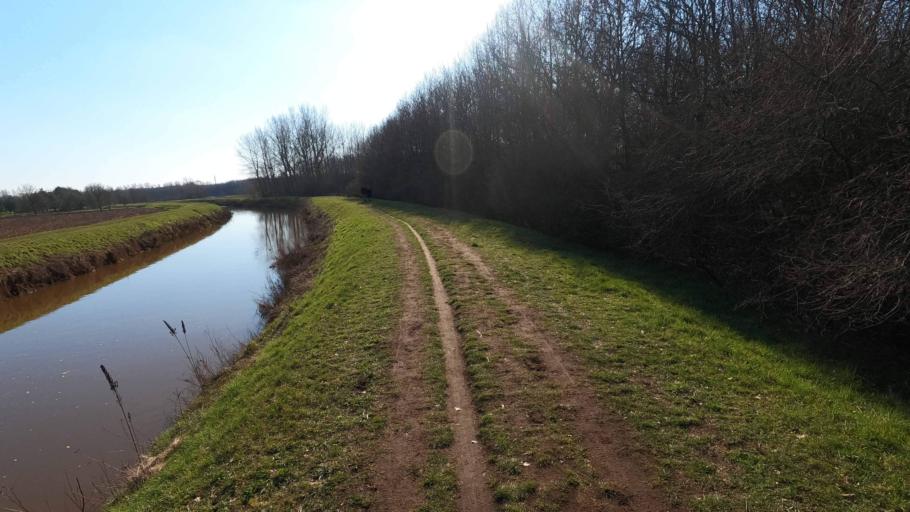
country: BE
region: Flanders
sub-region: Provincie Antwerpen
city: Herenthout
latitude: 51.1161
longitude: 4.7335
